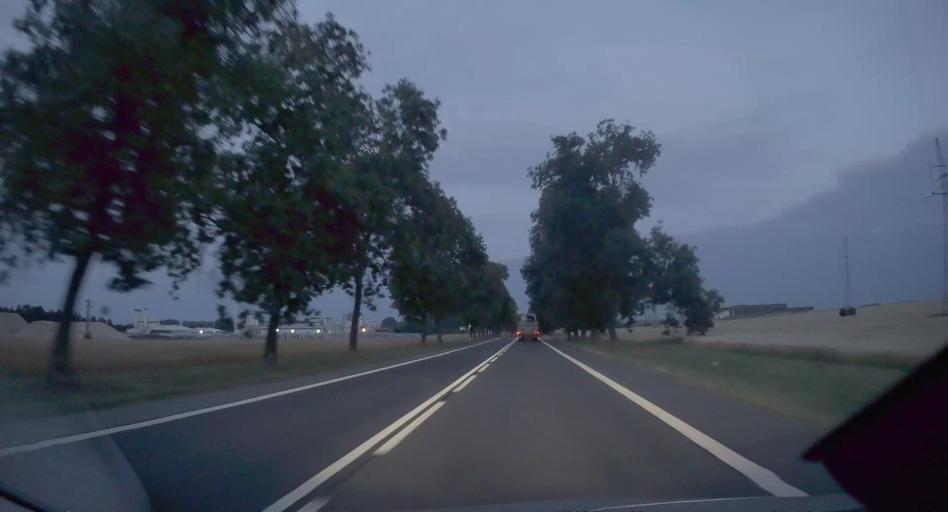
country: PL
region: Silesian Voivodeship
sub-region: Powiat klobucki
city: Klobuck
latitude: 50.9154
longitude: 18.8931
